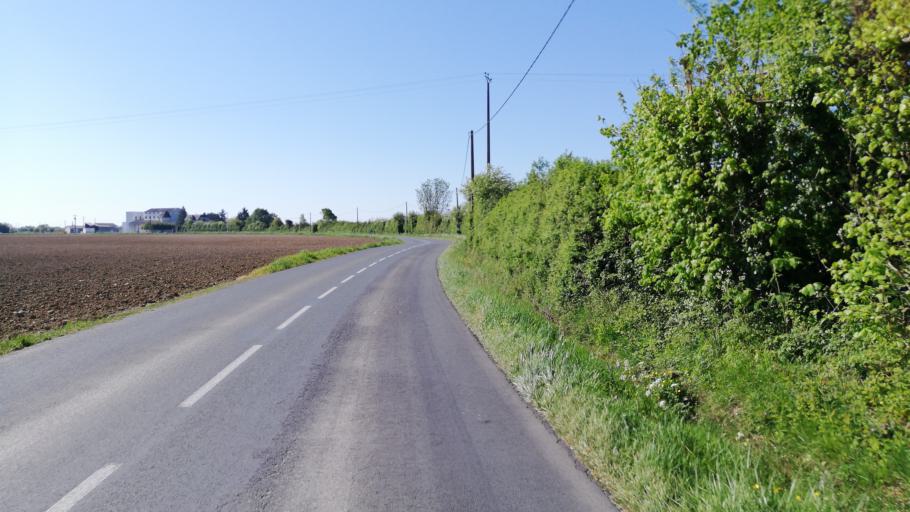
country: FR
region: Pays de la Loire
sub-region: Departement de la Vendee
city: Maillezais
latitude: 46.3296
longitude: -0.7438
